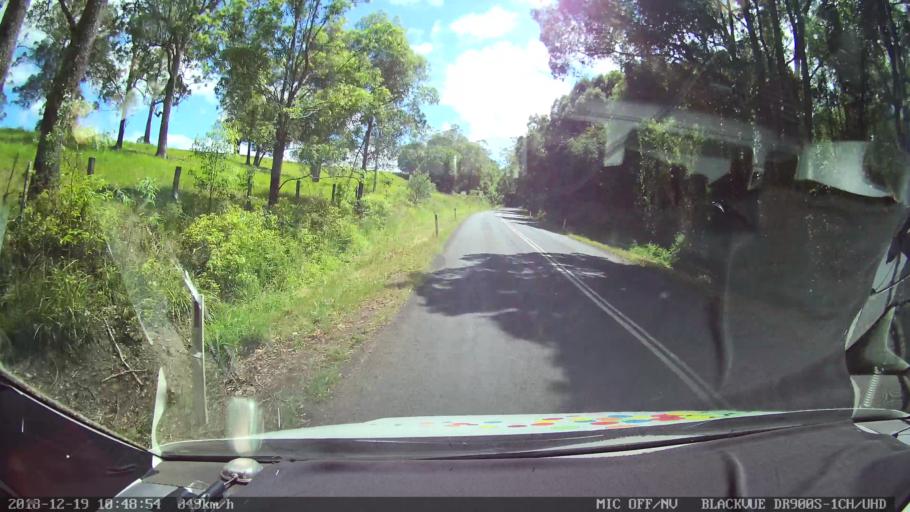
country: AU
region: New South Wales
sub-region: Lismore Municipality
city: Nimbin
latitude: -28.6034
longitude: 153.2152
